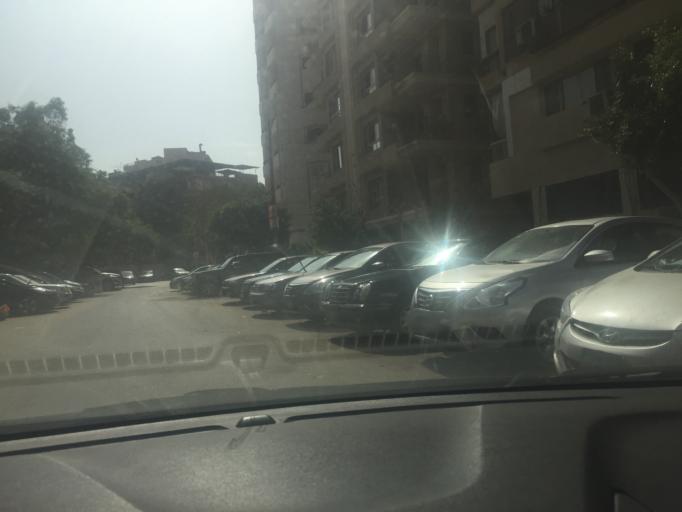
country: EG
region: Muhafazat al Qahirah
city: Cairo
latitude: 30.0865
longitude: 31.3458
